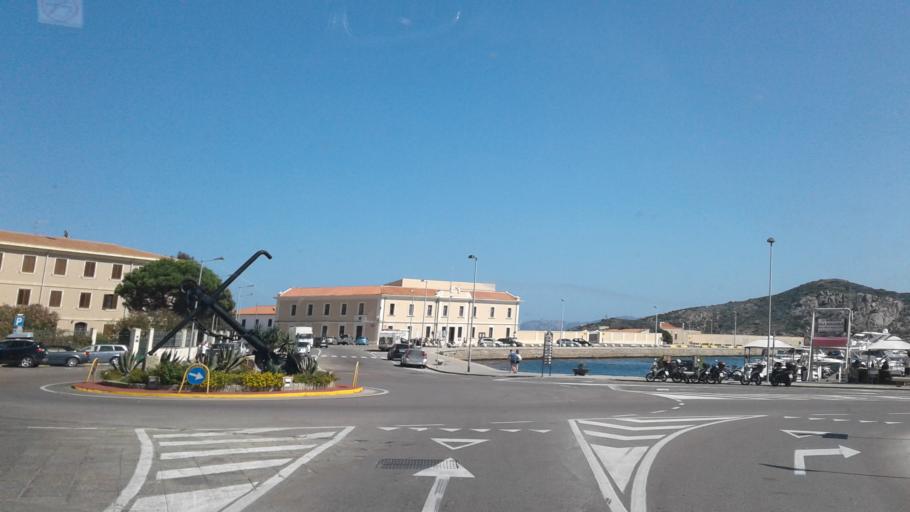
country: IT
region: Sardinia
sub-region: Provincia di Olbia-Tempio
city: La Maddalena
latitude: 41.2152
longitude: 9.4103
